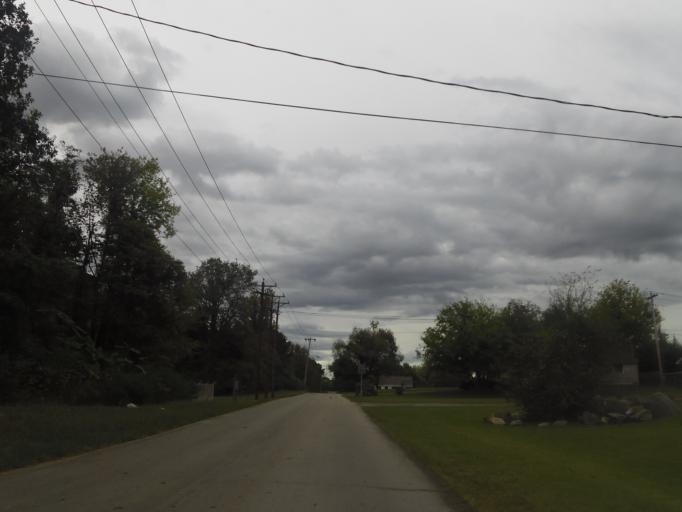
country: US
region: Tennessee
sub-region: Blount County
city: Alcoa
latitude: 35.7785
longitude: -83.9623
